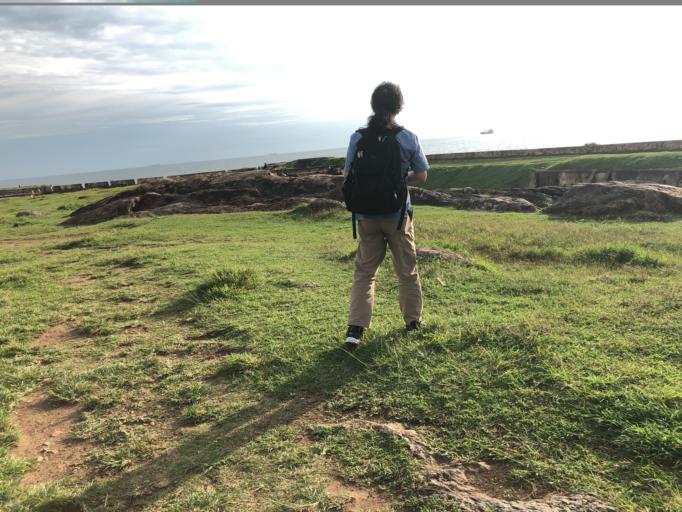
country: LK
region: Southern
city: Galle
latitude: 6.0281
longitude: 80.2145
